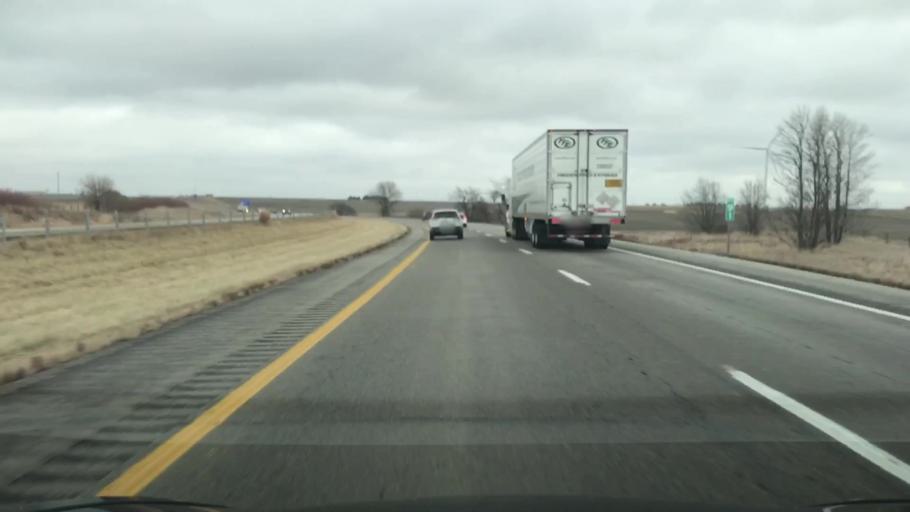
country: US
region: Iowa
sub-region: Guthrie County
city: Stuart
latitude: 41.4937
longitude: -94.3622
